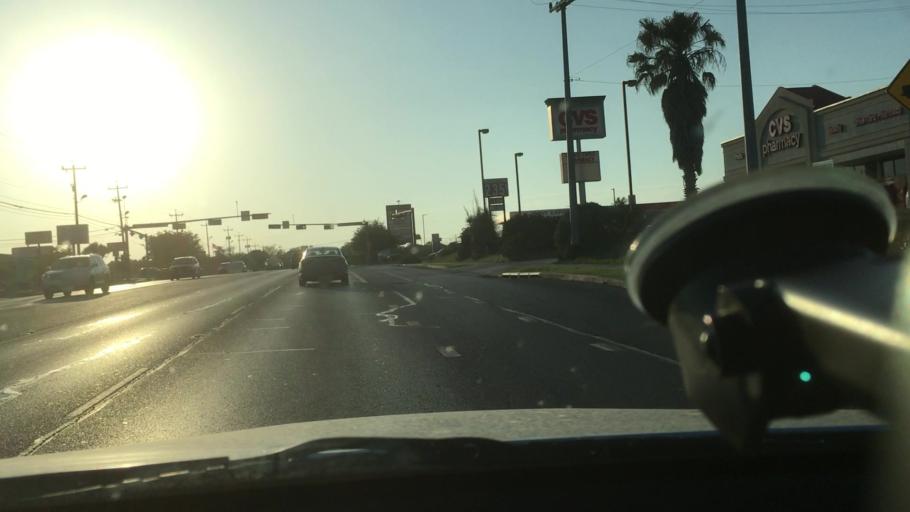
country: US
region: Texas
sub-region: Bexar County
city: Universal City
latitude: 29.5533
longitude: -98.3083
